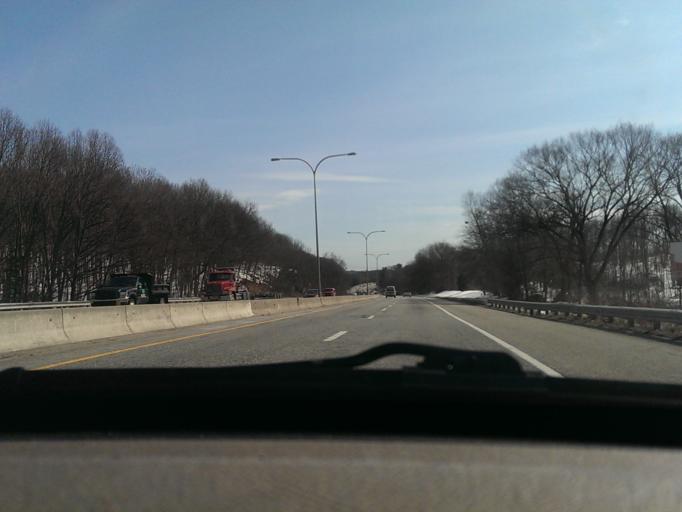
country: US
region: Rhode Island
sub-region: Providence County
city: North Providence
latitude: 41.8813
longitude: -71.4358
